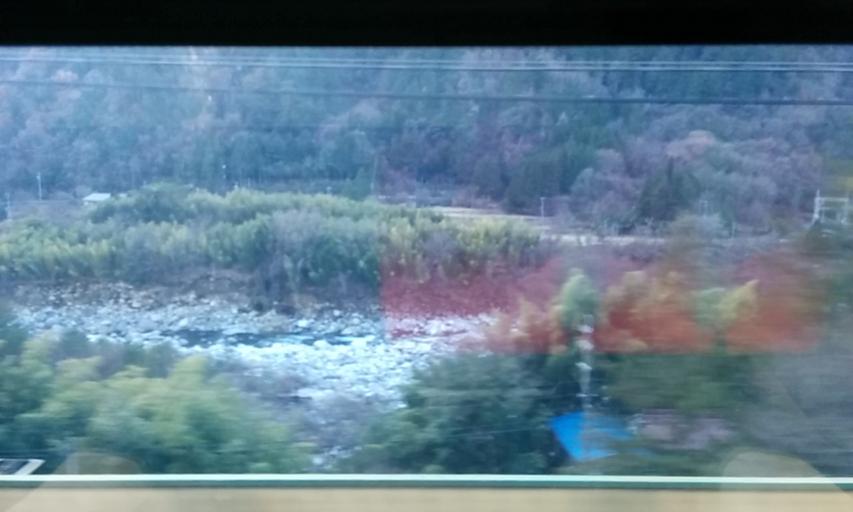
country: JP
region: Nagano
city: Ina
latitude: 35.7618
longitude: 137.7075
